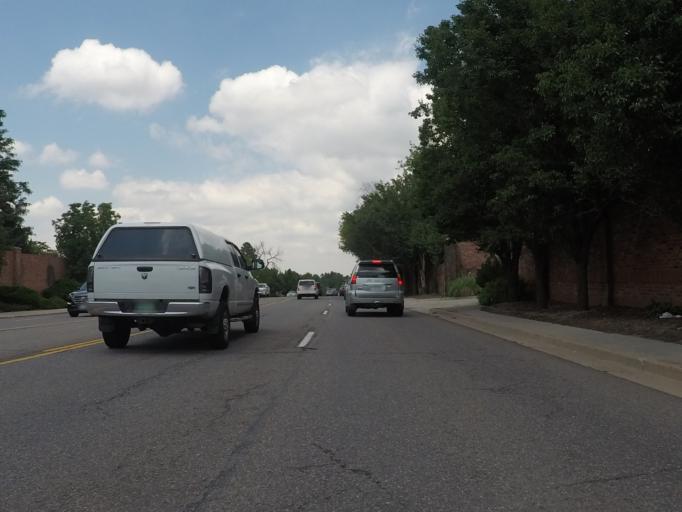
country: US
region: Colorado
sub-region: Arapahoe County
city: Greenwood Village
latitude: 39.6181
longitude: -104.9598
